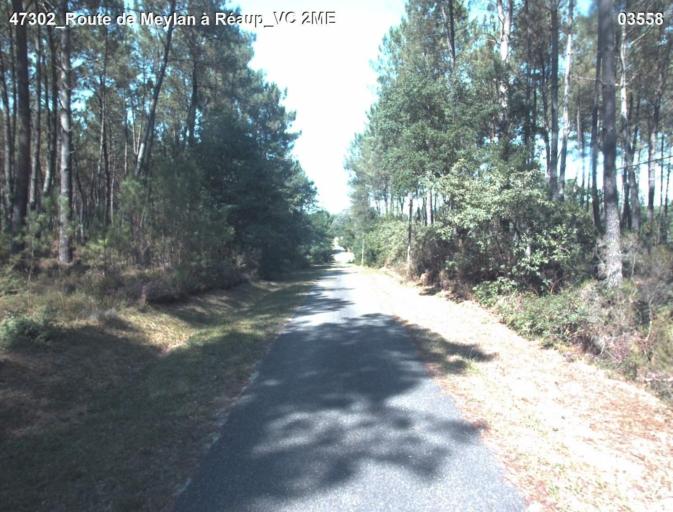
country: FR
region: Aquitaine
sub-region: Departement du Lot-et-Garonne
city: Mezin
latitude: 44.0786
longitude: 0.1241
